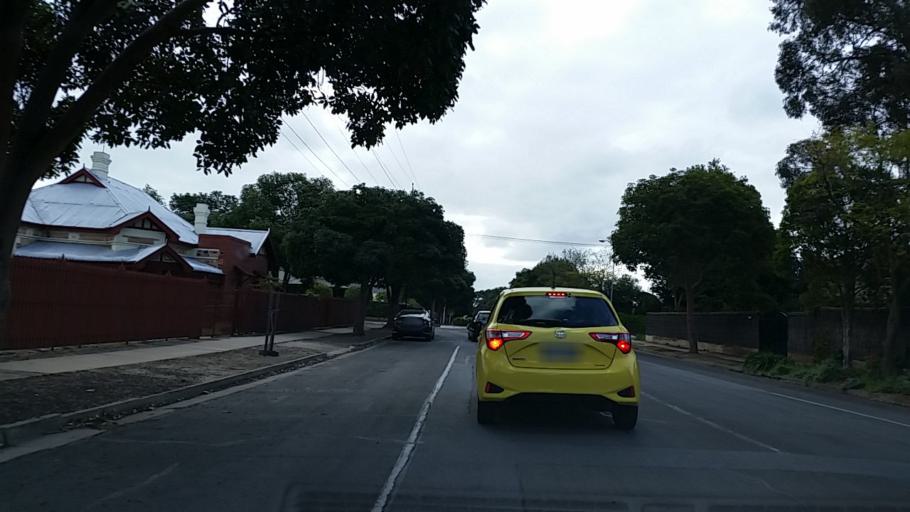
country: AU
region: South Australia
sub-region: Norwood Payneham St Peters
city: Royston Park
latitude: -34.9011
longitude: 138.6324
